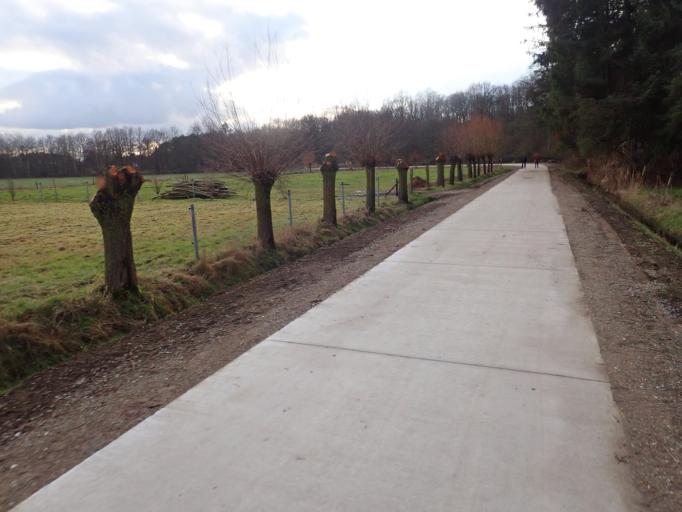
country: BE
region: Flanders
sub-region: Provincie Antwerpen
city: Schilde
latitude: 51.2220
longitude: 4.6165
